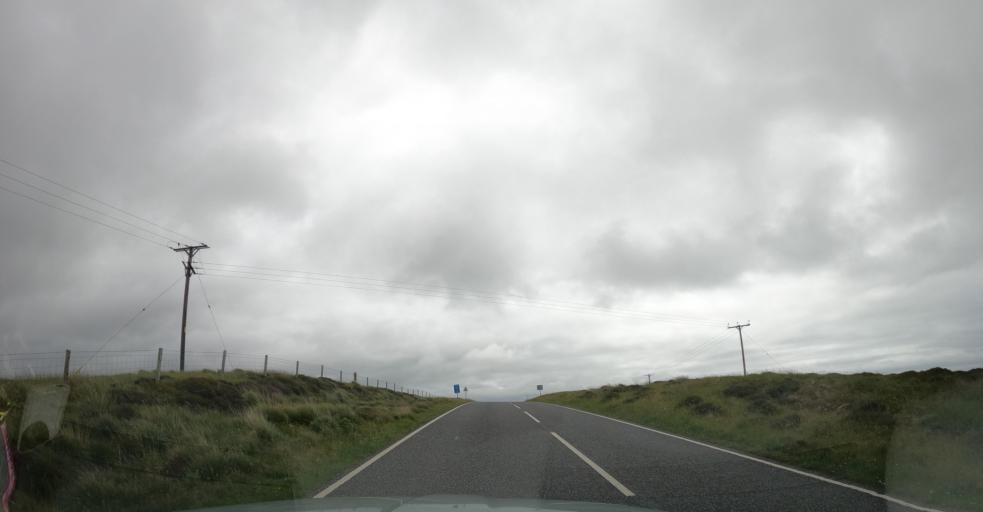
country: GB
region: Scotland
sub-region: Eilean Siar
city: Isle of North Uist
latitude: 57.5491
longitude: -7.3284
